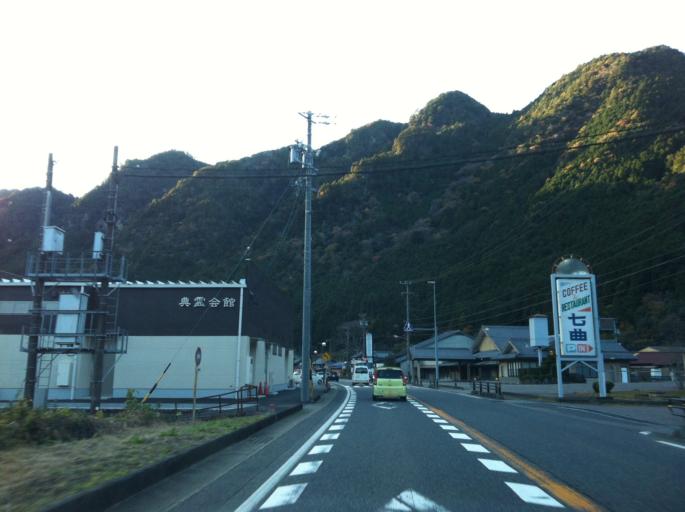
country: JP
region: Gifu
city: Minokamo
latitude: 35.6031
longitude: 137.1640
